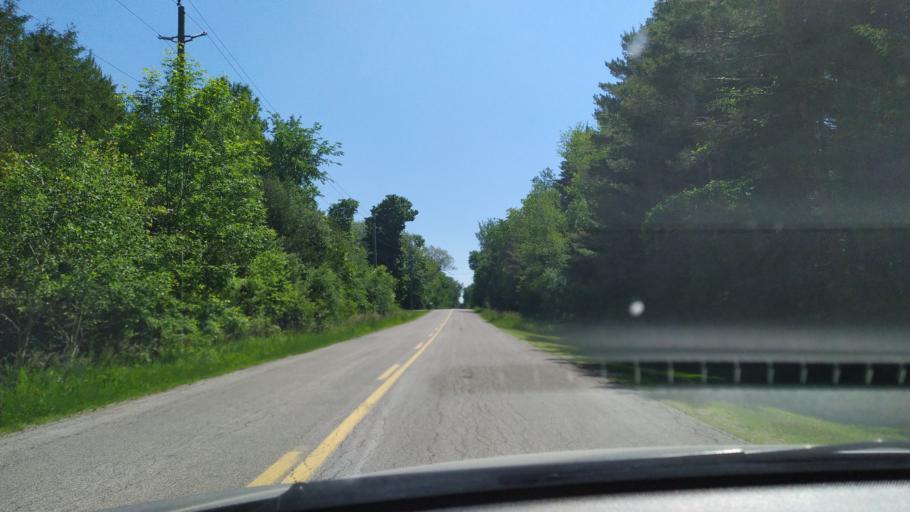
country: CA
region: Ontario
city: Waterloo
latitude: 43.4647
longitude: -80.6789
